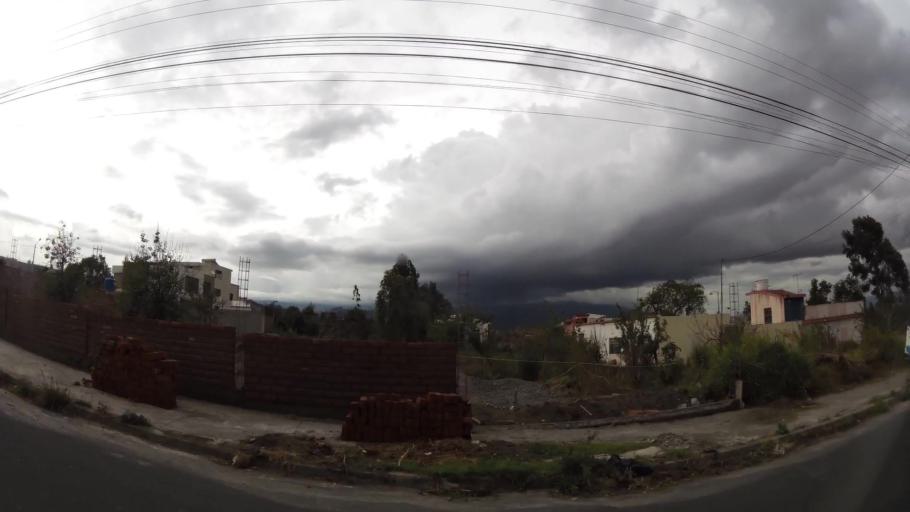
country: EC
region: Tungurahua
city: Ambato
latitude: -1.2804
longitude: -78.6214
